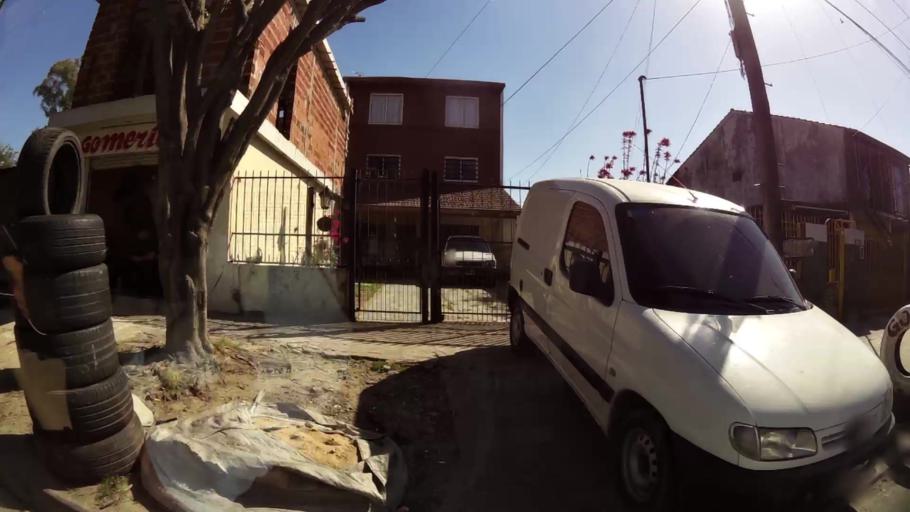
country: AR
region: Buenos Aires
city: Caseros
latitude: -34.5441
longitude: -58.5873
